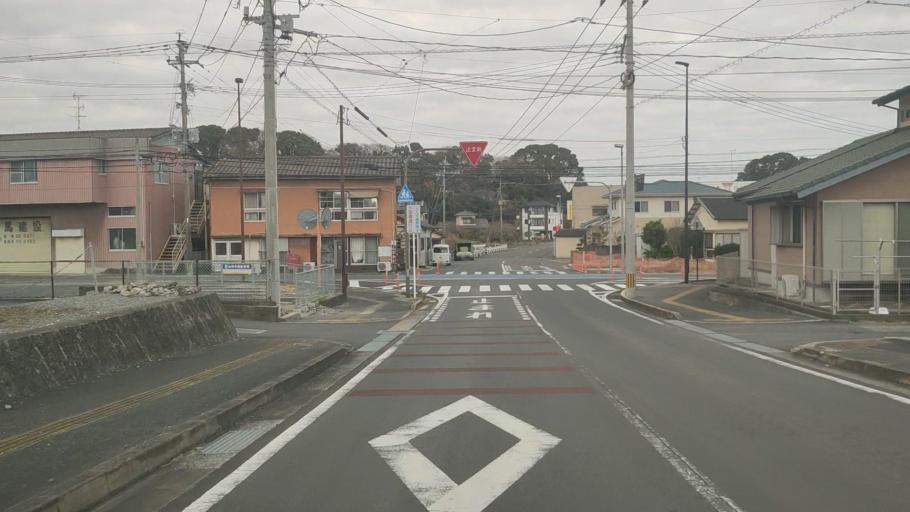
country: JP
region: Nagasaki
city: Shimabara
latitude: 32.7628
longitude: 130.3650
